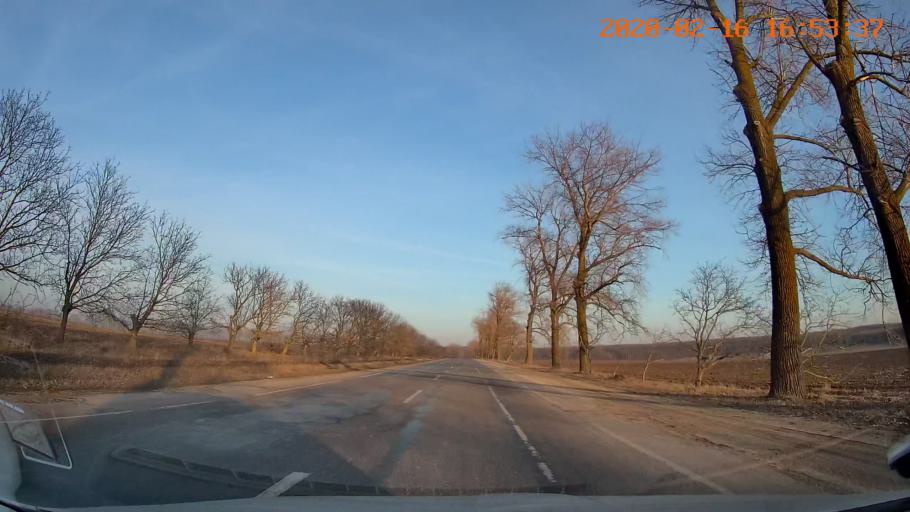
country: MD
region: Briceni
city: Briceni
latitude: 48.3163
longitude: 26.9888
